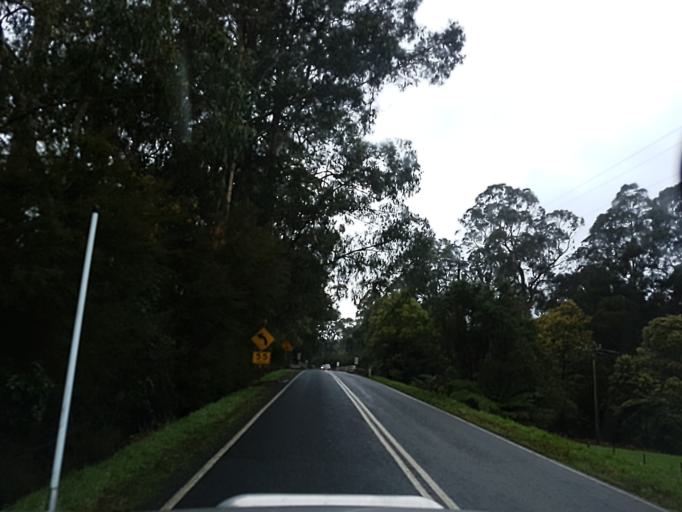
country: AU
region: Victoria
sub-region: Yarra Ranges
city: Millgrove
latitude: -37.7505
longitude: 145.7290
